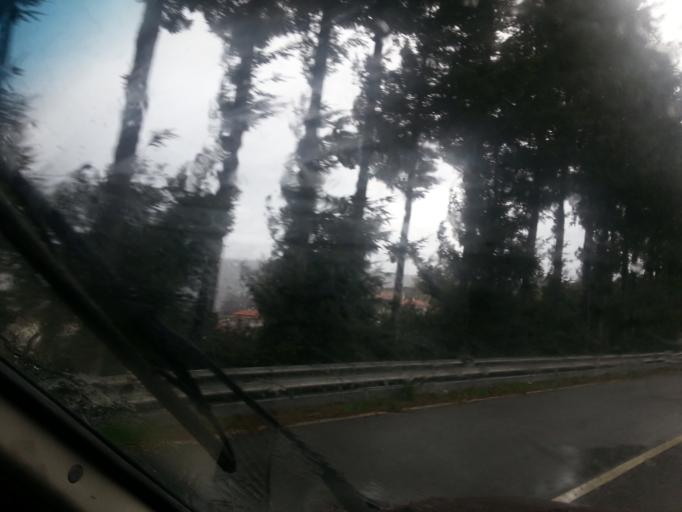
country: PT
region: Guarda
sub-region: Guarda
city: Guarda
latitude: 40.5431
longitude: -7.3174
